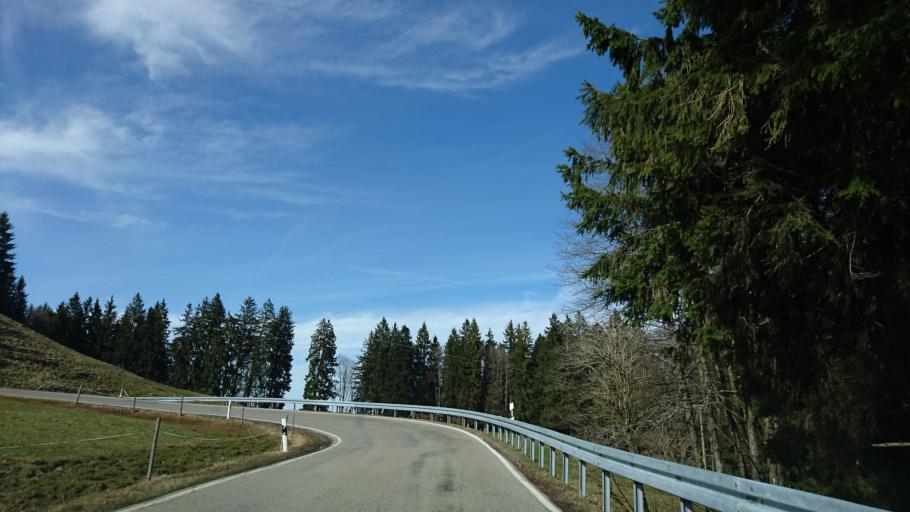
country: DE
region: Bavaria
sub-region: Upper Bavaria
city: Bernbeuren
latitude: 47.7353
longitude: 10.7379
